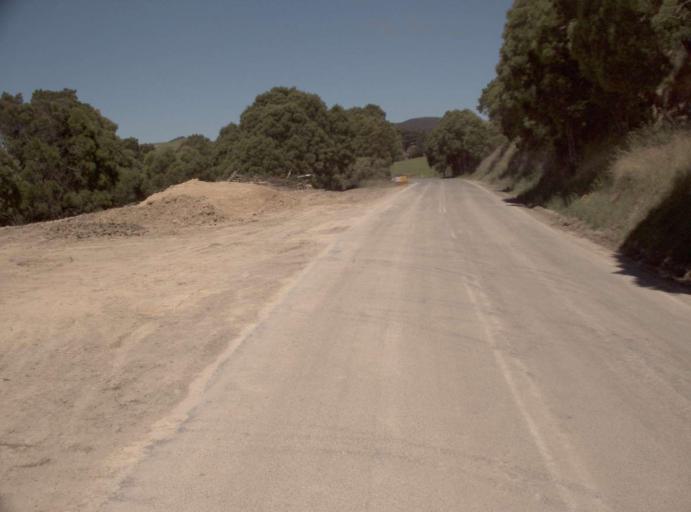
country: AU
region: Victoria
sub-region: Bass Coast
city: North Wonthaggi
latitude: -38.6953
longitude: 146.0992
